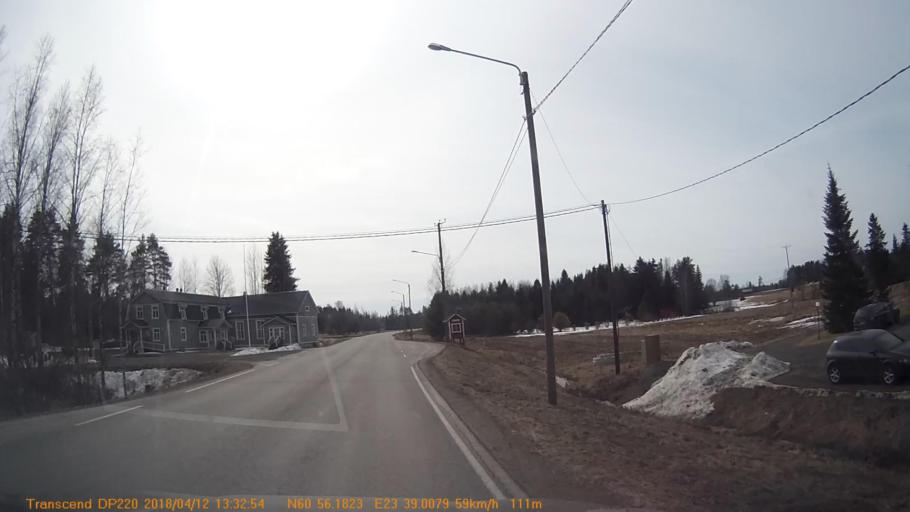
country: FI
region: Haeme
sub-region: Forssa
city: Forssa
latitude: 60.9363
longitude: 23.6501
